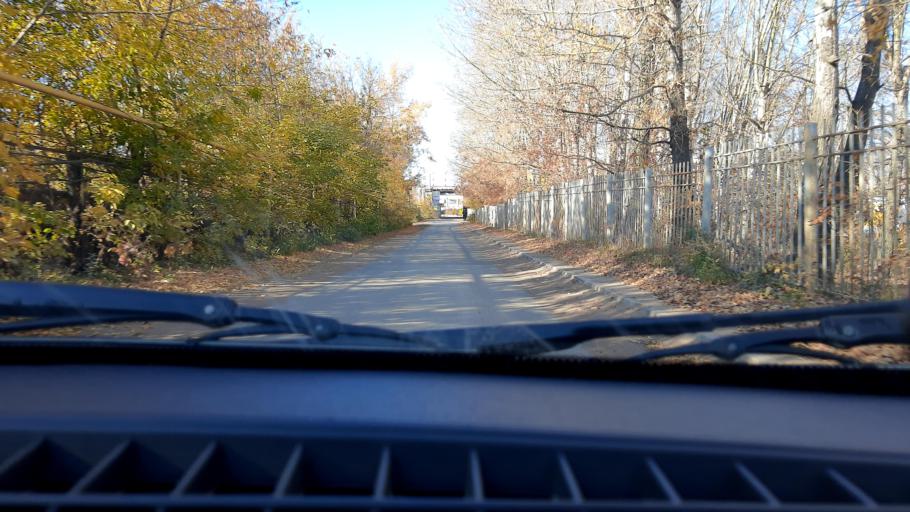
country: RU
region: Bashkortostan
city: Ufa
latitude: 54.8357
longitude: 56.1166
